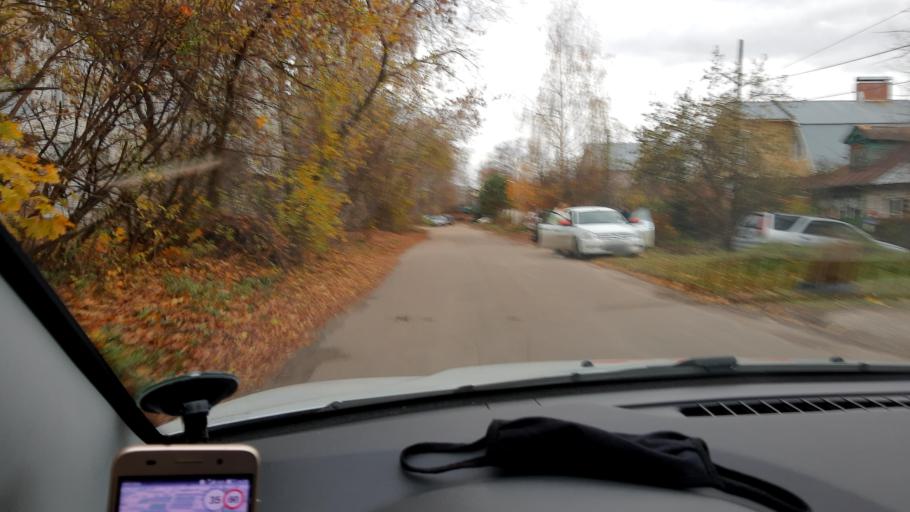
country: RU
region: Nizjnij Novgorod
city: Gorbatovka
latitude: 56.3597
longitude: 43.8437
